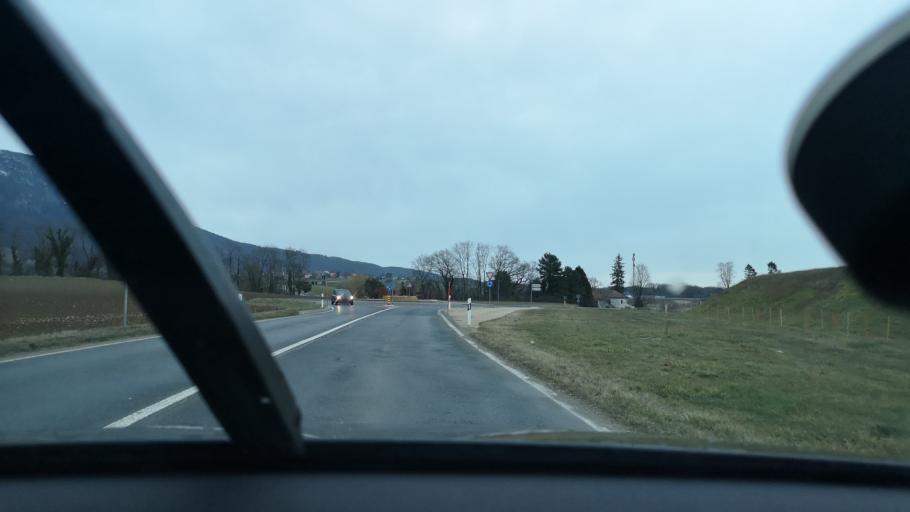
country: CH
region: Vaud
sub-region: Jura-Nord vaudois District
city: Grandson
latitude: 46.8272
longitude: 6.6729
